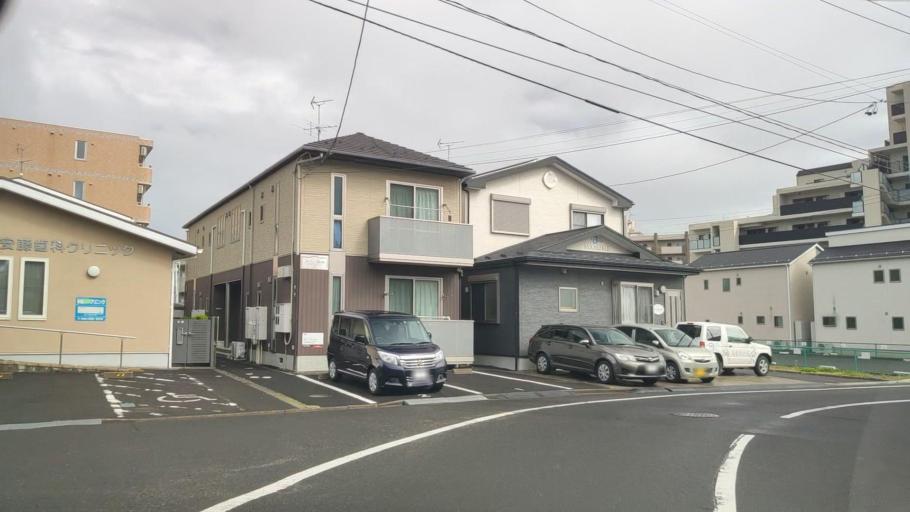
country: JP
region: Miyagi
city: Sendai
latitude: 38.2444
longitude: 140.8892
